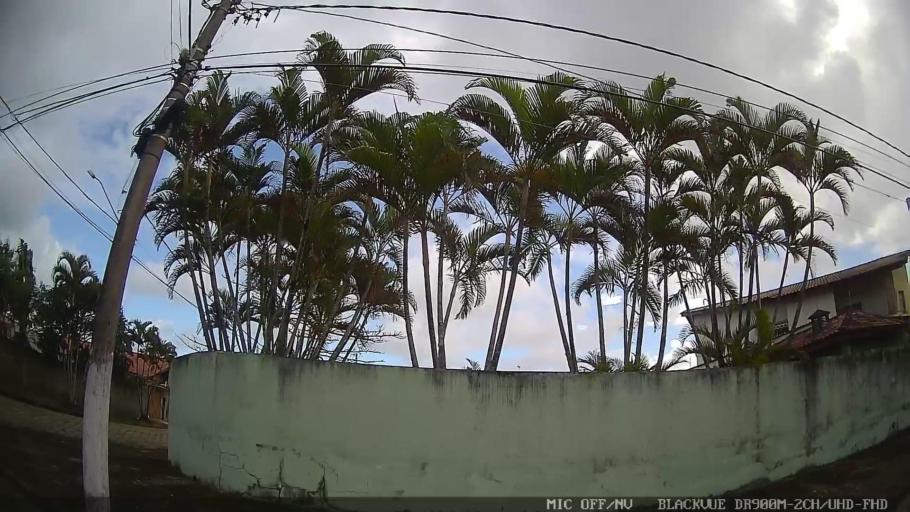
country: BR
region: Sao Paulo
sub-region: Itanhaem
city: Itanhaem
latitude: -24.2207
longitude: -46.8522
